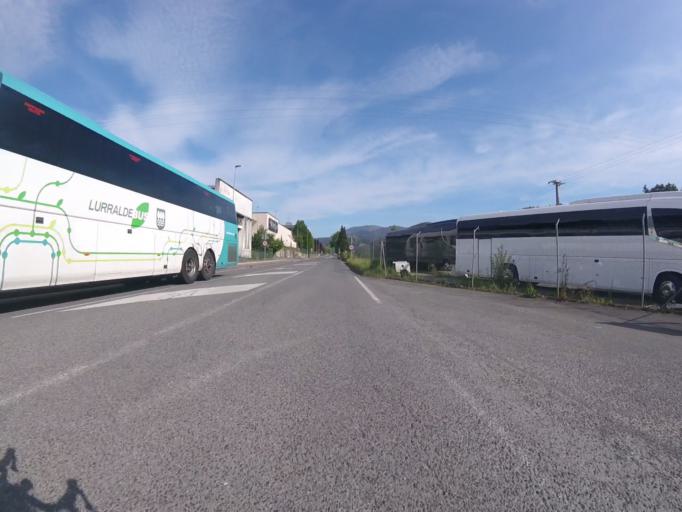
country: ES
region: Basque Country
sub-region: Provincia de Guipuzcoa
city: Ormaiztegui
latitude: 43.0475
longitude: -2.2603
